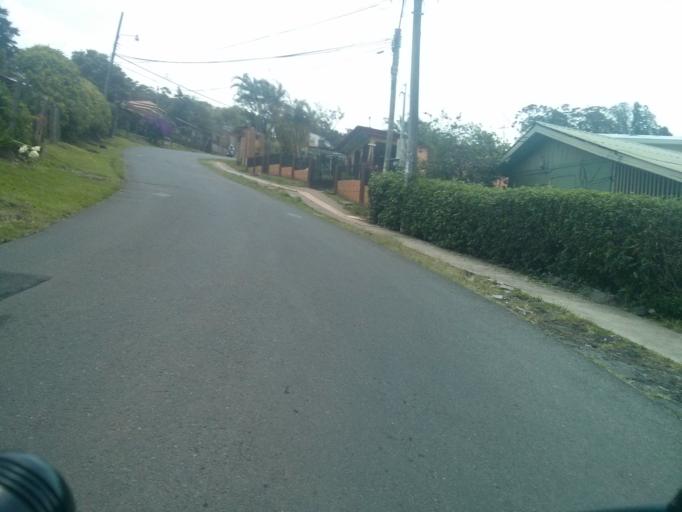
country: CR
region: Heredia
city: Angeles
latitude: 10.0228
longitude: -84.0390
